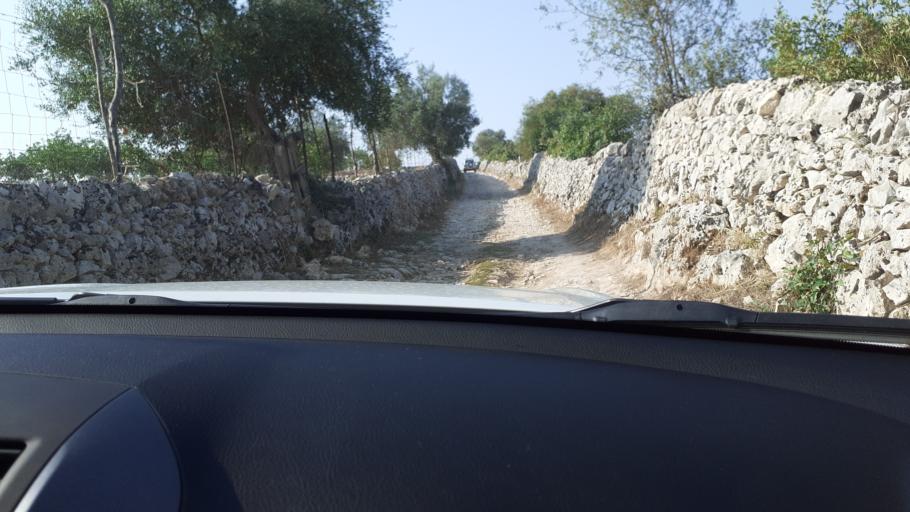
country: IT
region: Sicily
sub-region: Provincia di Siracusa
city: Canicattini Bagni
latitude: 36.9818
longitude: 15.0923
